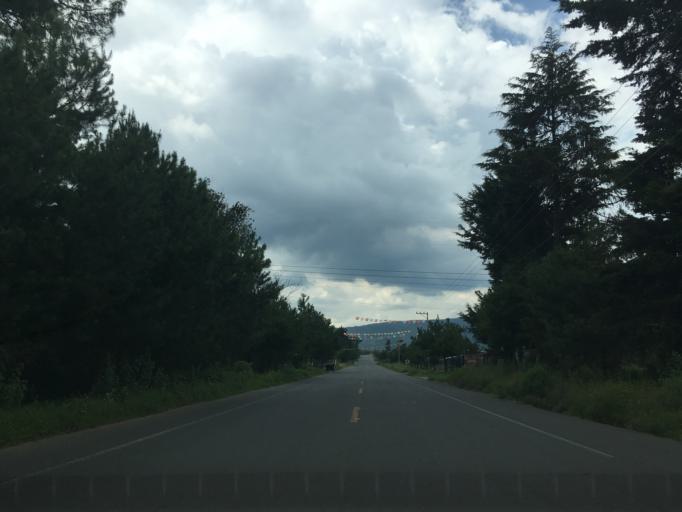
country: MX
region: Michoacan
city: Capacuaro
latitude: 19.5317
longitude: -102.0884
